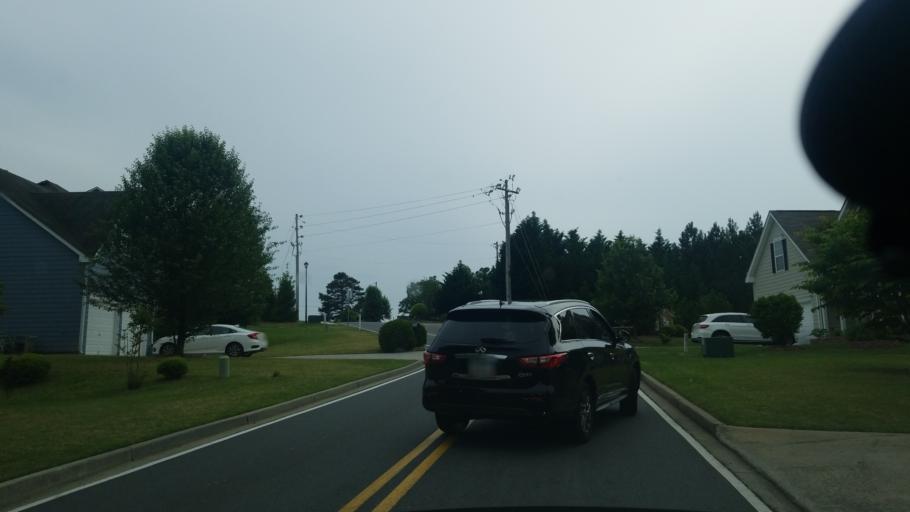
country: US
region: Georgia
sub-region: Forsyth County
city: Cumming
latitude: 34.1240
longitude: -84.1252
